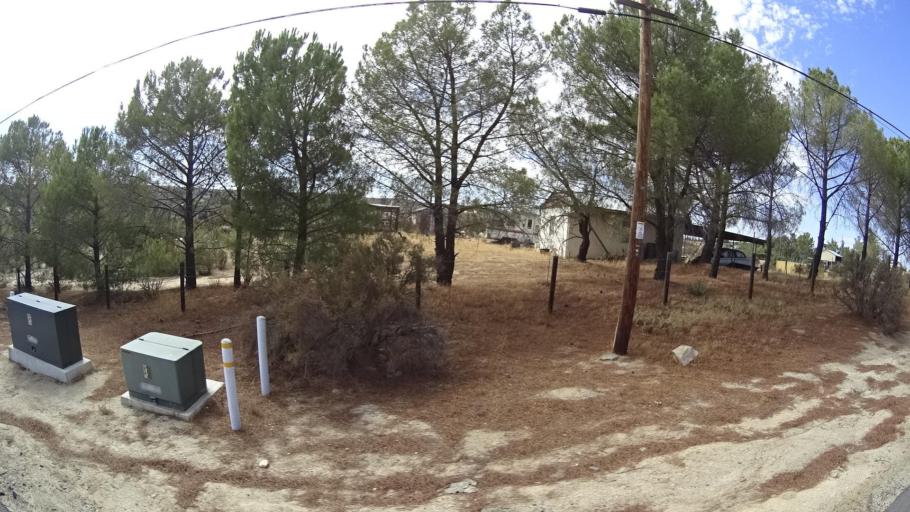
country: MX
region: Baja California
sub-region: Tecate
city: Cereso del Hongo
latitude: 32.6556
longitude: -116.2907
